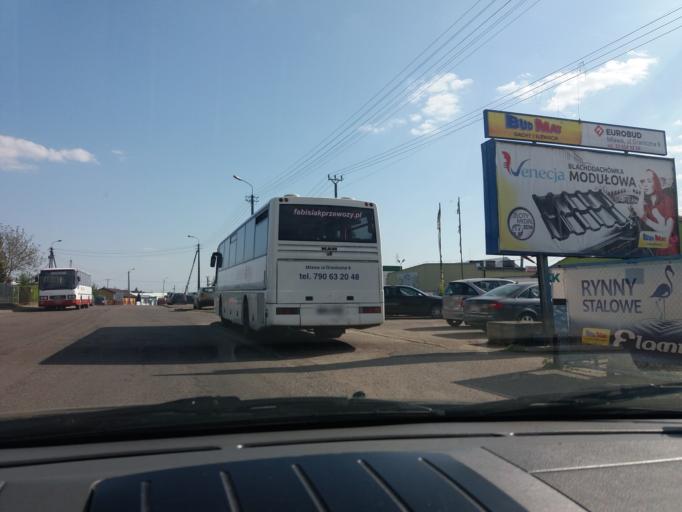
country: PL
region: Masovian Voivodeship
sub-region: Powiat mlawski
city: Mlawa
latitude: 53.1189
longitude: 20.3583
